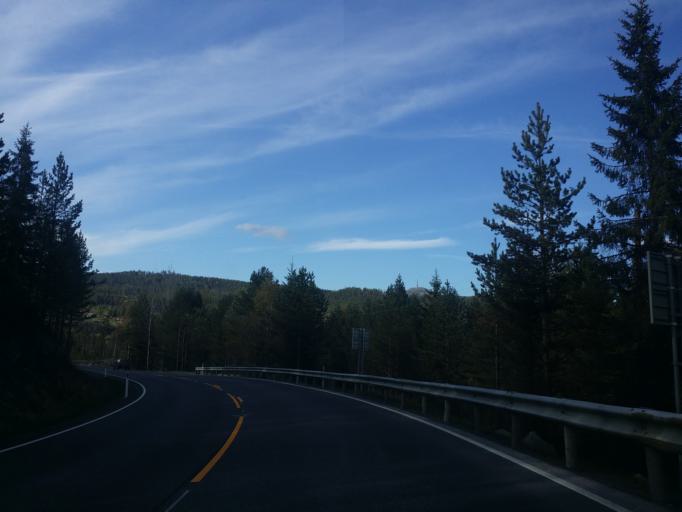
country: NO
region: Buskerud
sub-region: Kongsberg
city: Kongsberg
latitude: 59.6198
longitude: 9.4743
